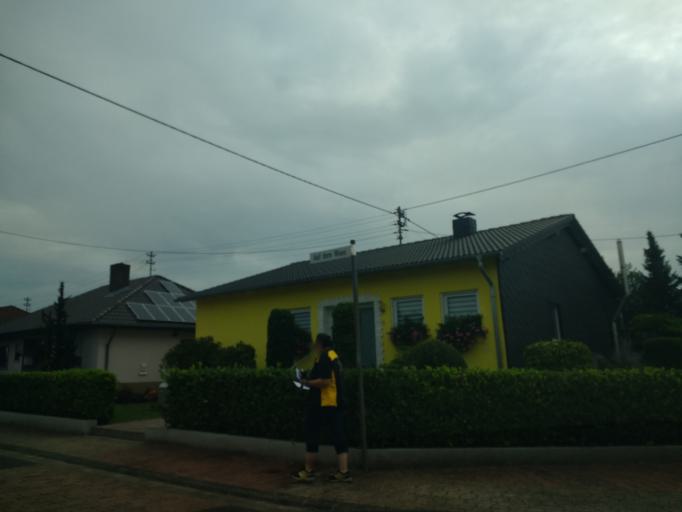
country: DE
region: Rheinland-Pfalz
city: Kirf
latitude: 49.4989
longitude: 6.4418
